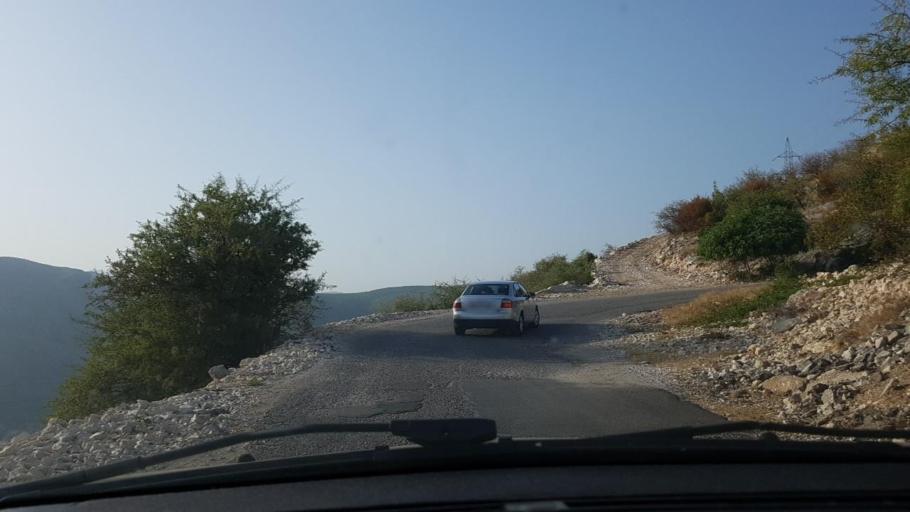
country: BA
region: Federation of Bosnia and Herzegovina
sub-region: Hercegovacko-Bosanski Kanton
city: Mostar
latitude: 43.3518
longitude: 17.8262
